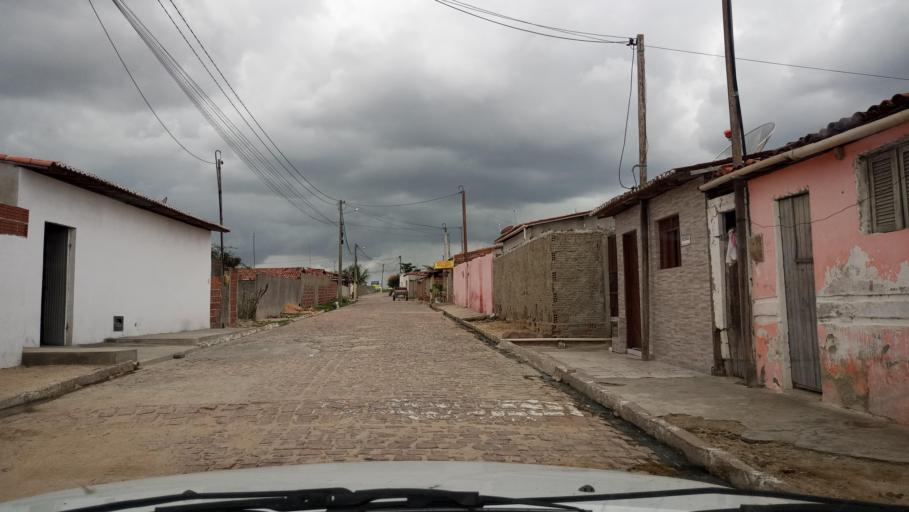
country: BR
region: Rio Grande do Norte
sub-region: Tangara
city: Tangara
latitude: -6.1001
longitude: -35.7127
